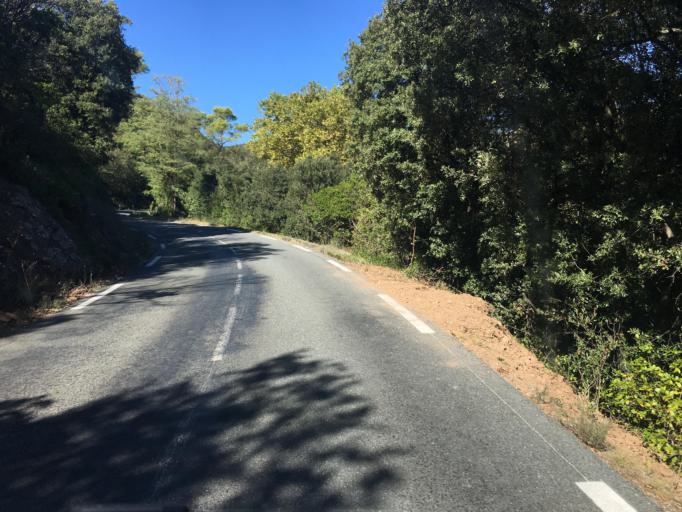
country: FR
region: Languedoc-Roussillon
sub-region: Departement de l'Herault
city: Nebian
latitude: 43.6122
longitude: 3.3806
